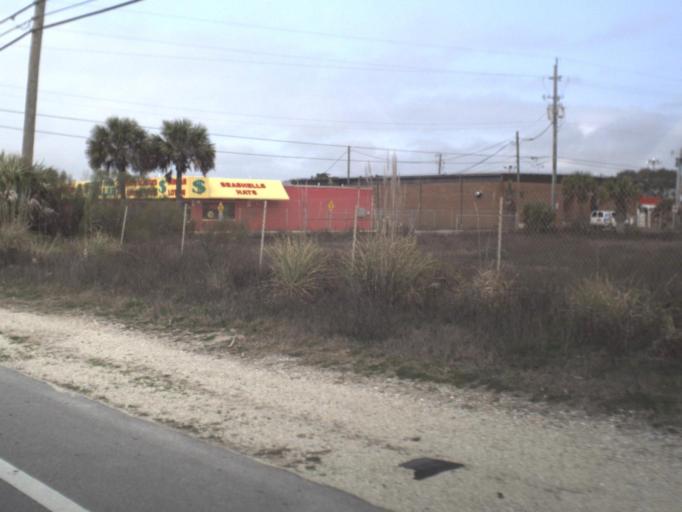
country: US
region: Florida
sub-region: Bay County
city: Panama City Beach
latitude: 30.2034
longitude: -85.8536
